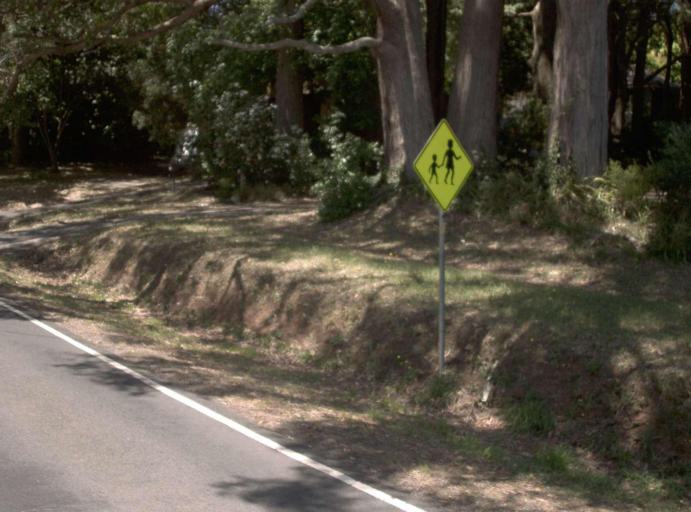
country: AU
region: Victoria
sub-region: Yarra Ranges
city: Ferny Creek
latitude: -37.8720
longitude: 145.3450
